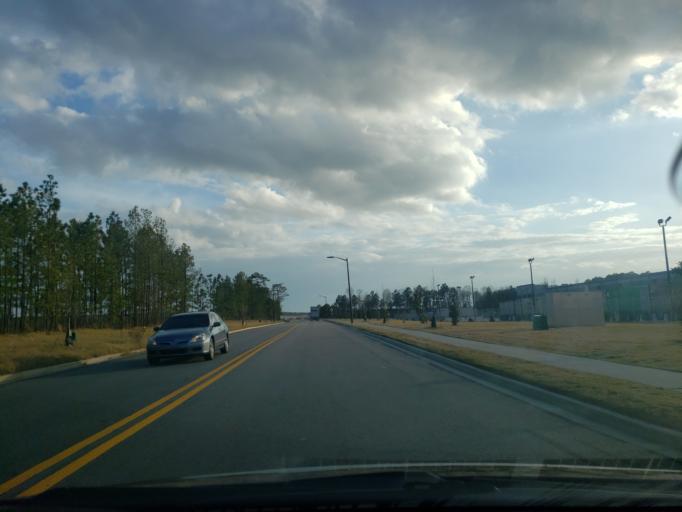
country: US
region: Georgia
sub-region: Chatham County
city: Bloomingdale
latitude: 32.1718
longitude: -81.2700
